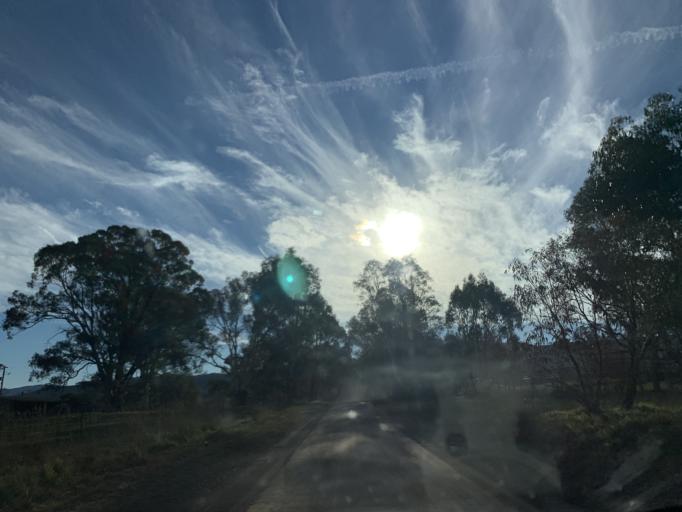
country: AU
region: Victoria
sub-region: Mansfield
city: Mansfield
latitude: -36.9600
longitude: 146.1035
